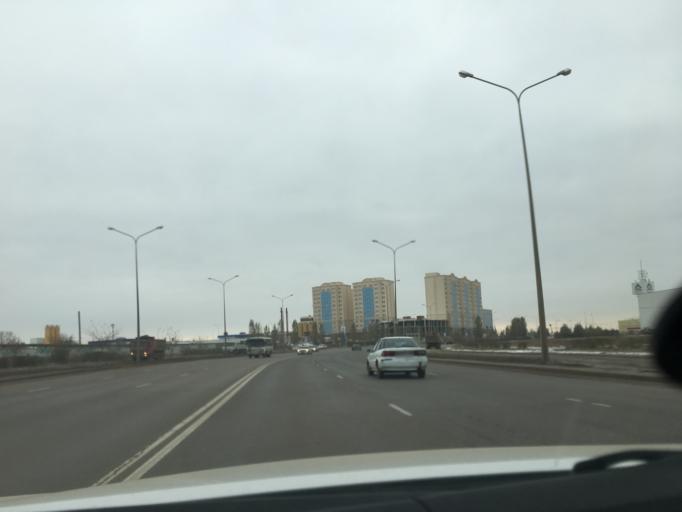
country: KZ
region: Astana Qalasy
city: Astana
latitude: 51.1476
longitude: 71.5300
